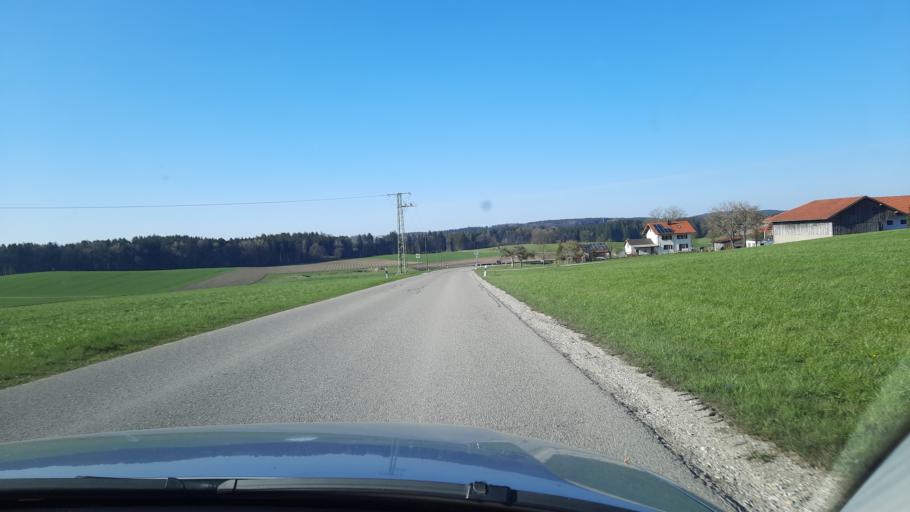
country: DE
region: Bavaria
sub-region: Upper Bavaria
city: Kirchseeon
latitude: 48.0503
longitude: 11.8966
